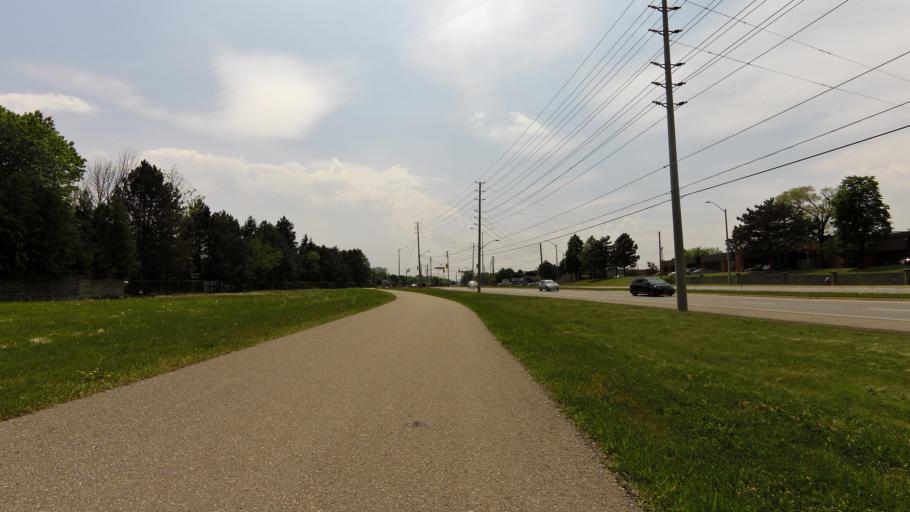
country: CA
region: Ontario
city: Mississauga
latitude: 43.5871
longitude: -79.5934
